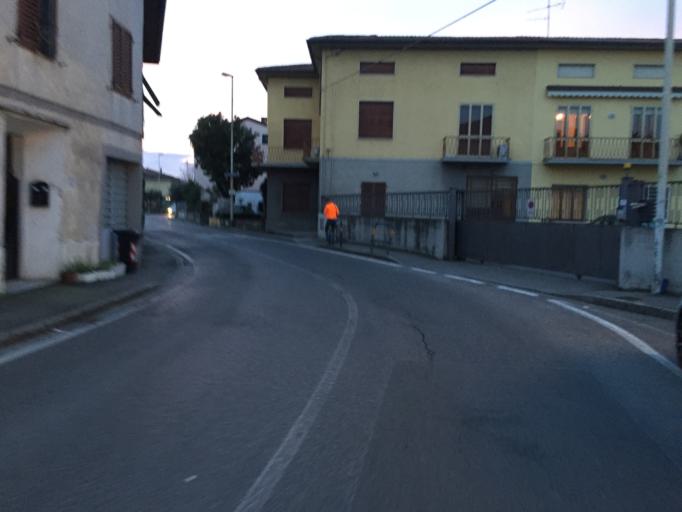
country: IT
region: Tuscany
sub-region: Provincia di Prato
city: Prato
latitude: 43.8844
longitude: 11.0536
